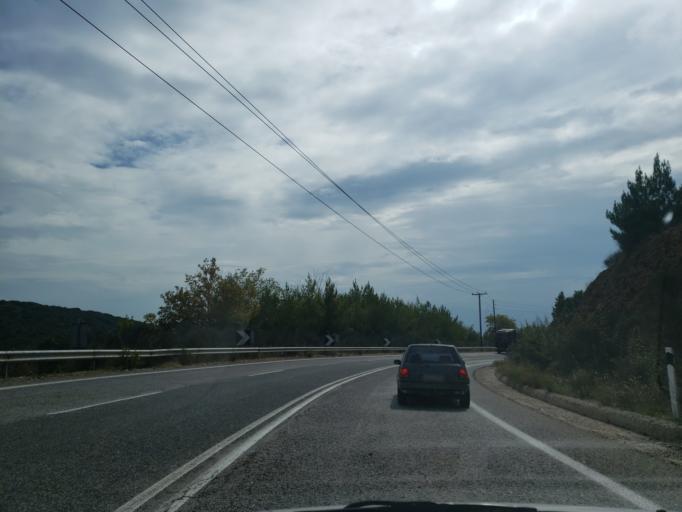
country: GR
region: Central Greece
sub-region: Nomos Fthiotidos
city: Stavros
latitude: 38.9854
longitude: 22.3795
